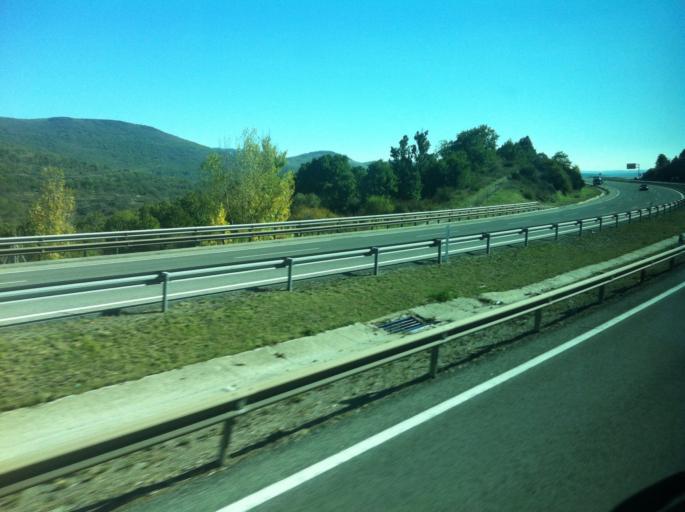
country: ES
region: Madrid
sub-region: Provincia de Madrid
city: Robregordo
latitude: 41.1040
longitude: -3.5926
